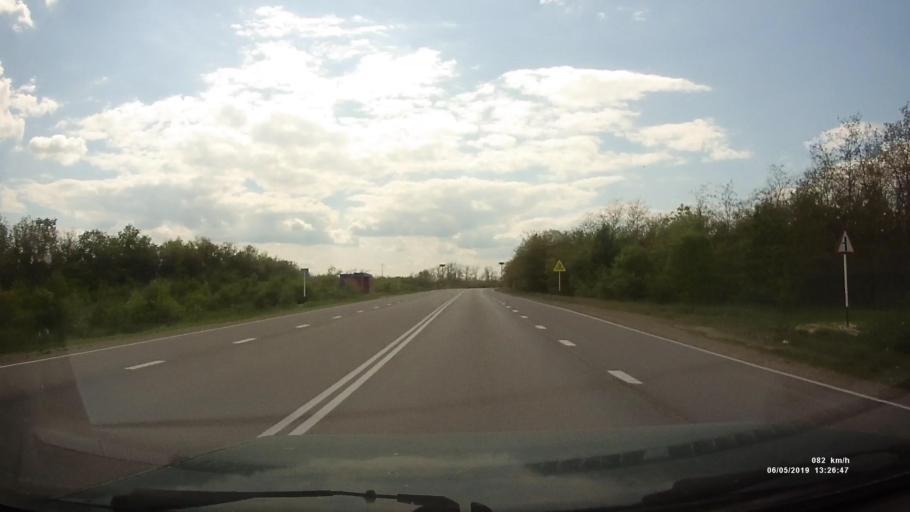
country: RU
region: Rostov
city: Ust'-Donetskiy
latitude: 47.6754
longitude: 40.8918
